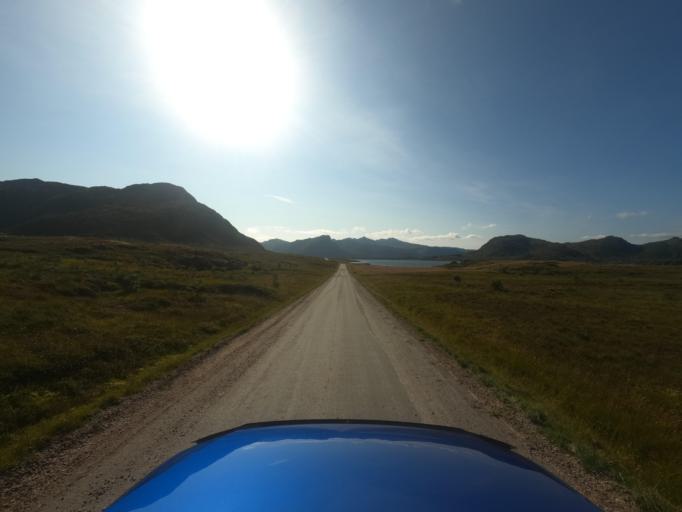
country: NO
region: Nordland
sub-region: Vestvagoy
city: Evjen
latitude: 68.2813
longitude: 13.7804
